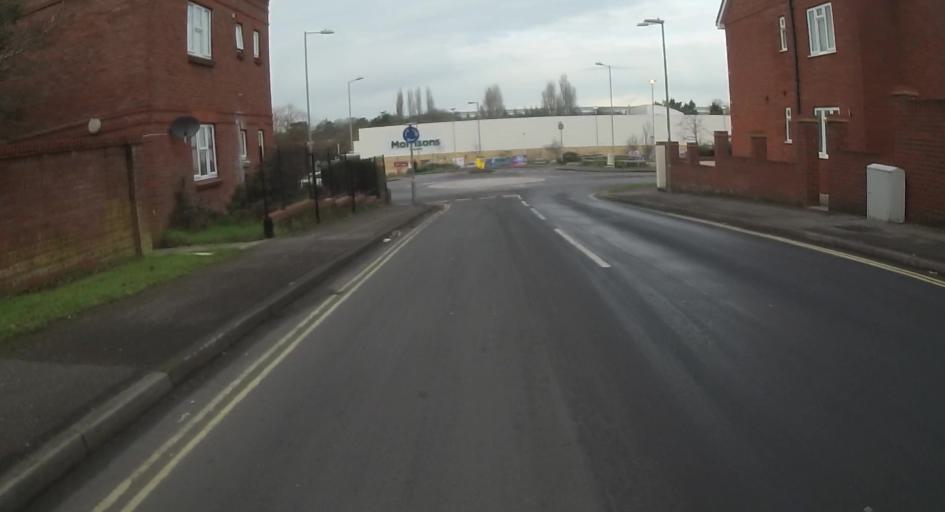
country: GB
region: England
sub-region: Hampshire
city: Basingstoke
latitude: 51.2624
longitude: -1.1031
